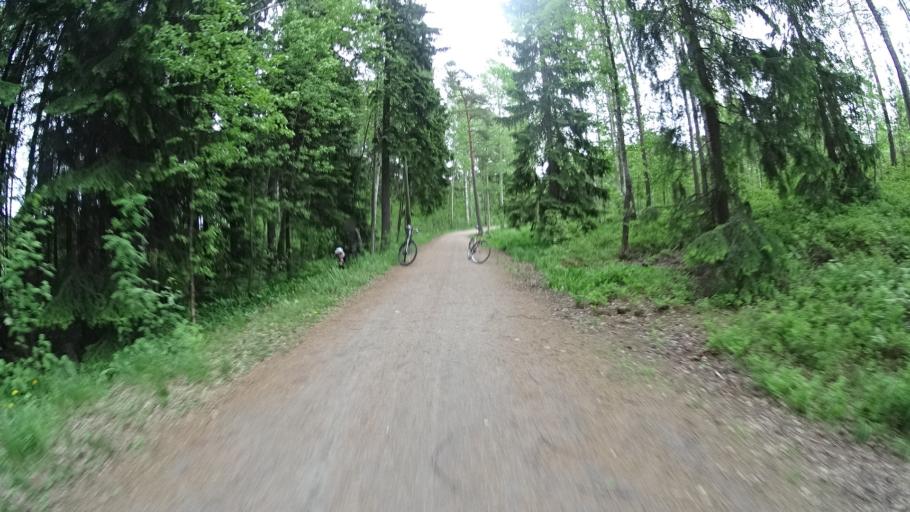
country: FI
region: Uusimaa
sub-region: Helsinki
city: Vantaa
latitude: 60.2517
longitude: 25.0701
